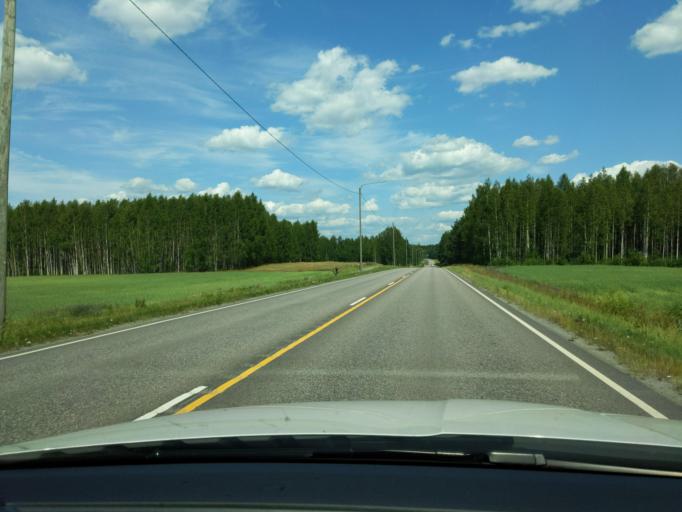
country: FI
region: Paijanne Tavastia
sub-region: Lahti
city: Heinola
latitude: 61.1446
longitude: 25.9729
